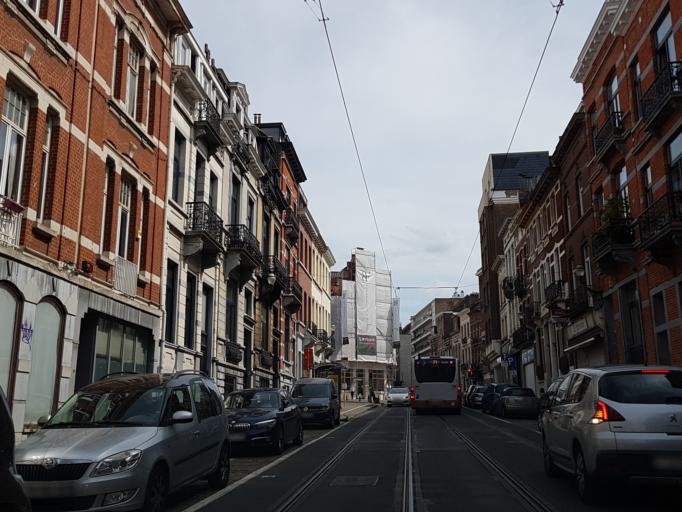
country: BE
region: Brussels Capital
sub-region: Bruxelles-Capitale
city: Brussels
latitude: 50.8213
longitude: 4.3763
